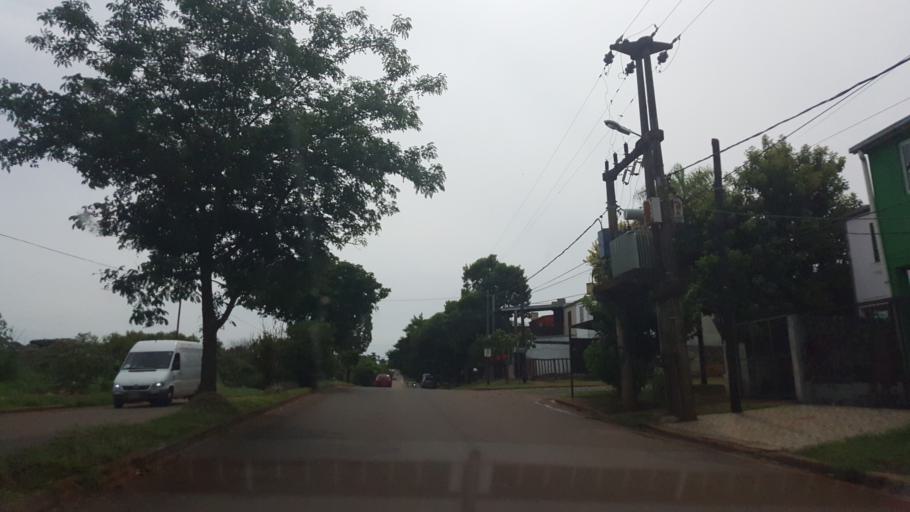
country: AR
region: Misiones
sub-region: Departamento de Capital
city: Posadas
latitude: -27.3879
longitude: -55.9422
